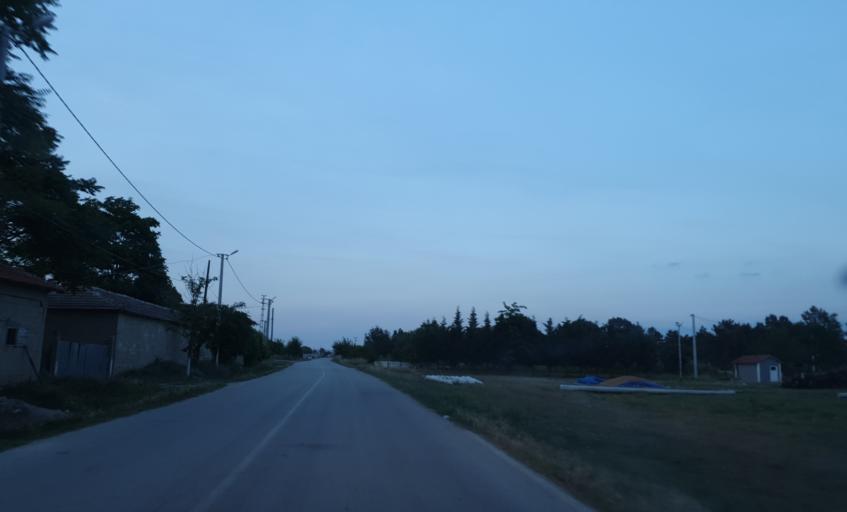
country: TR
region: Tekirdag
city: Beyazkoy
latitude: 41.4368
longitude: 27.6968
